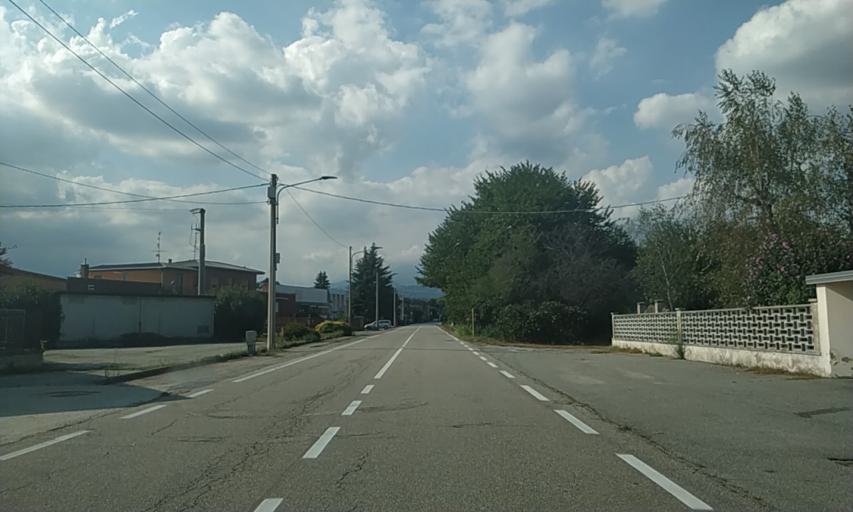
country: IT
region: Piedmont
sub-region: Provincia di Biella
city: Cerreto Castello
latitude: 45.5468
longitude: 8.1774
